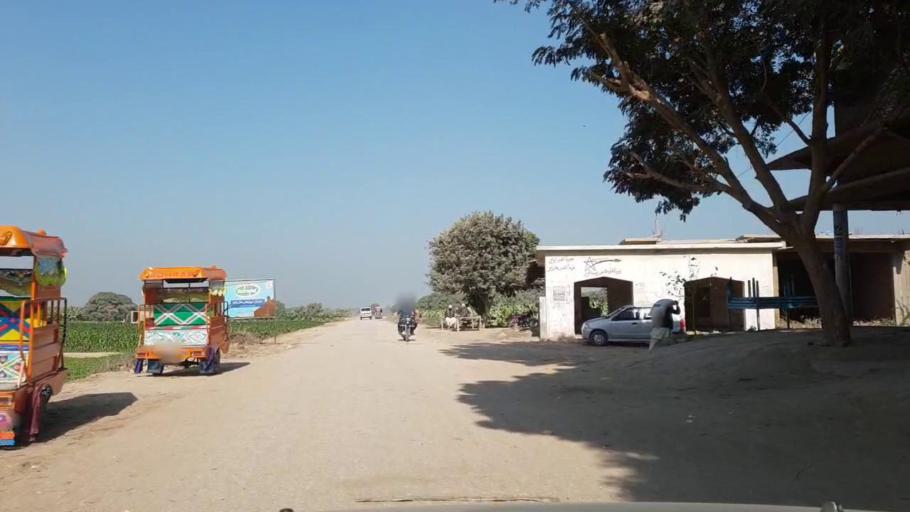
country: PK
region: Sindh
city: Matiari
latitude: 25.6096
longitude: 68.5966
